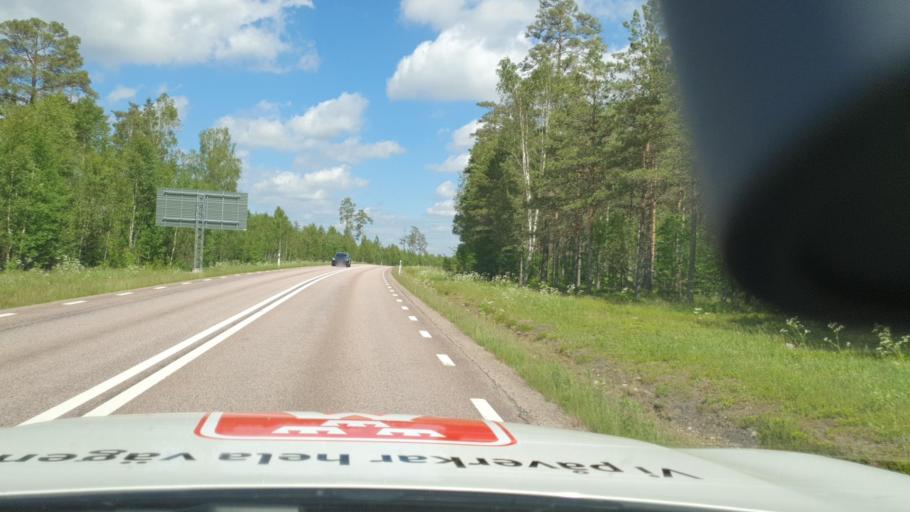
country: SE
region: Vaermland
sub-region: Filipstads Kommun
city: Filipstad
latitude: 59.6245
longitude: 13.9483
